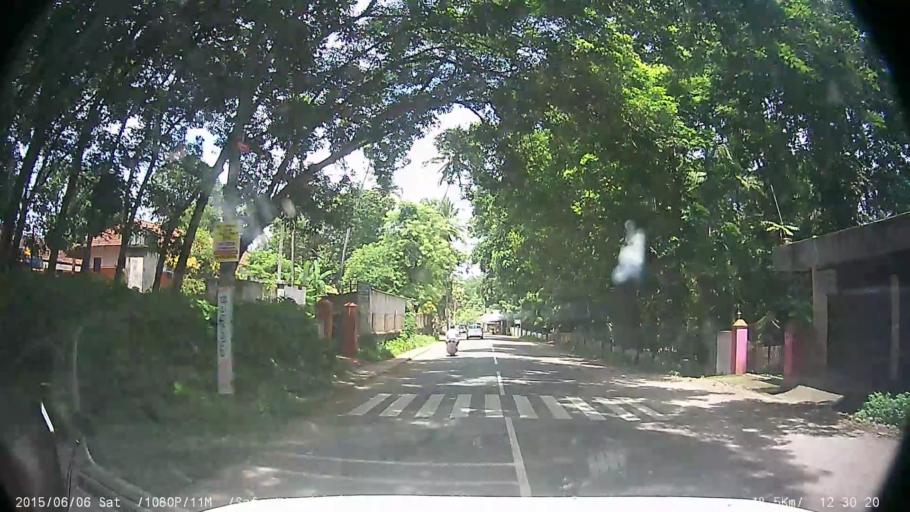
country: IN
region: Kerala
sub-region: Kottayam
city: Kottayam
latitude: 9.6248
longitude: 76.6036
